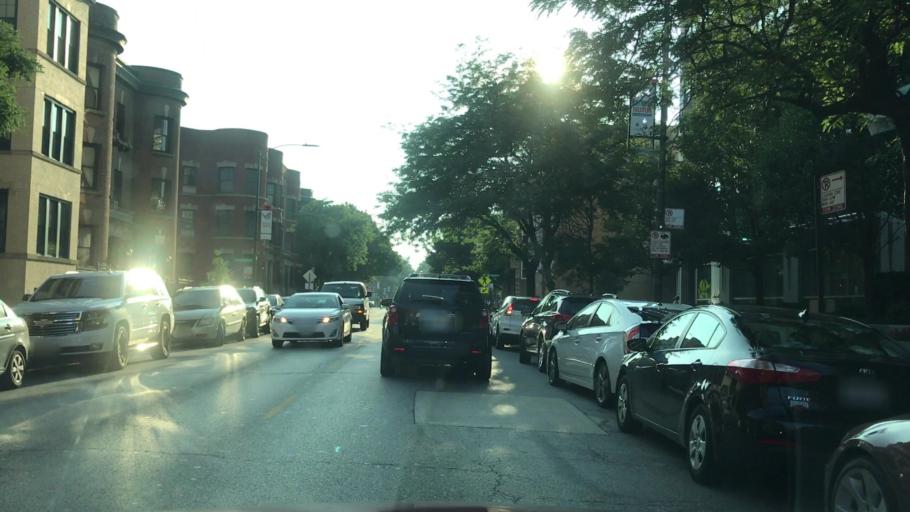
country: US
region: Illinois
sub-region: Cook County
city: Chicago
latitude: 41.9400
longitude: -87.6421
